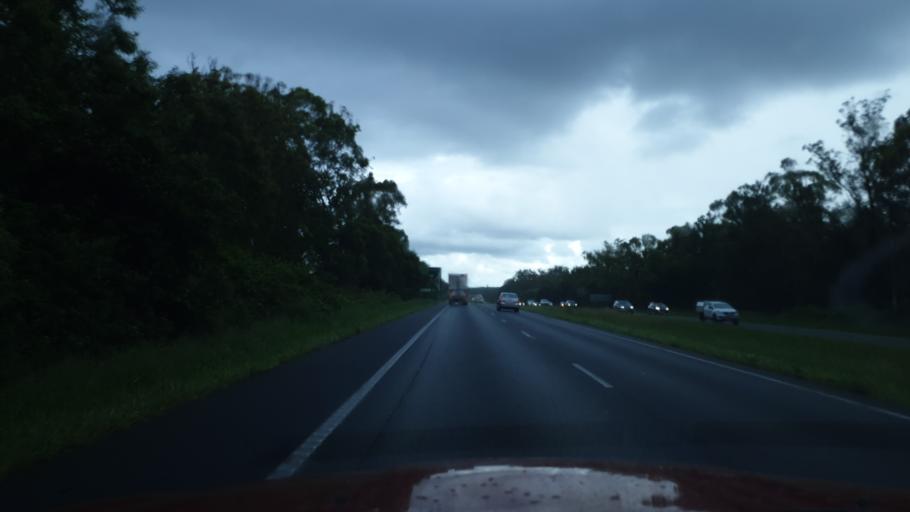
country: AU
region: Queensland
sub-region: Moreton Bay
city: Caboolture
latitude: -27.0034
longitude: 152.9773
